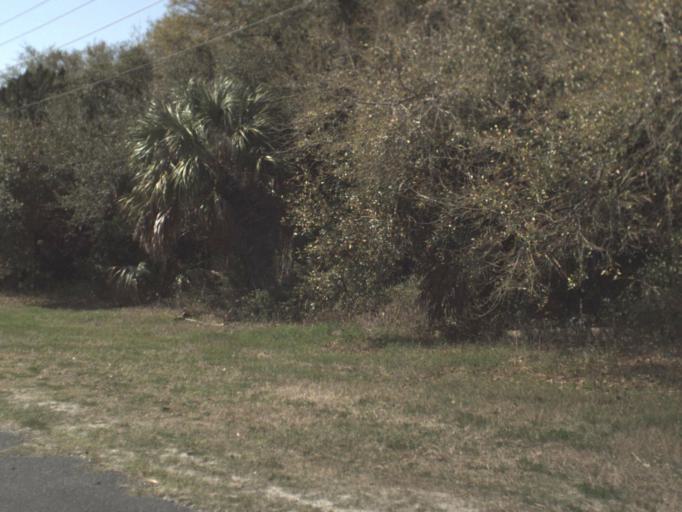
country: US
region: Florida
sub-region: Franklin County
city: Eastpoint
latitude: 29.7252
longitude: -84.8880
